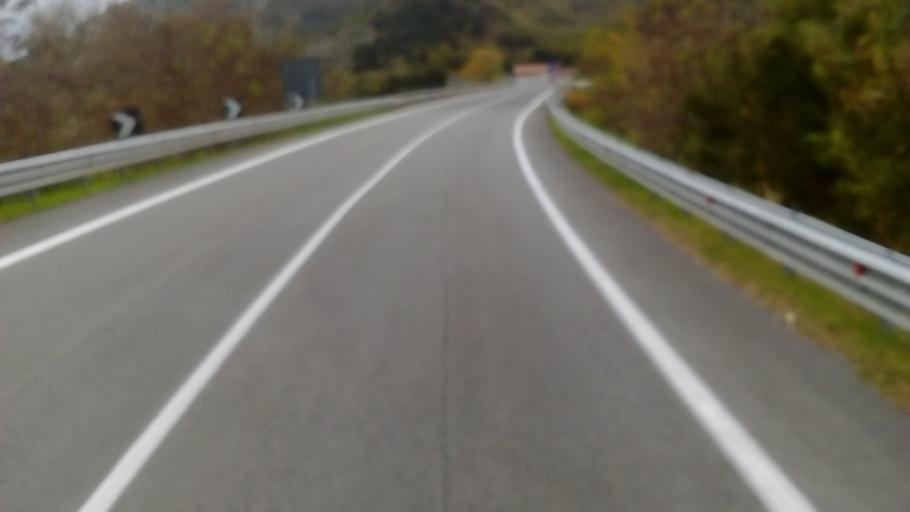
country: IT
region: Molise
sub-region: Provincia di Campobasso
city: Trivento
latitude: 41.7977
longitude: 14.5572
